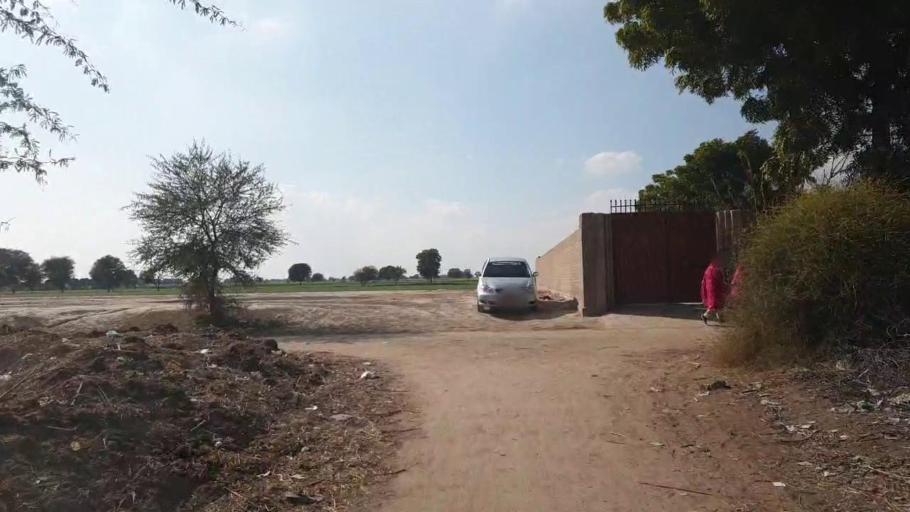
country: PK
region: Sindh
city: Shahpur Chakar
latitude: 26.1023
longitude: 68.5647
